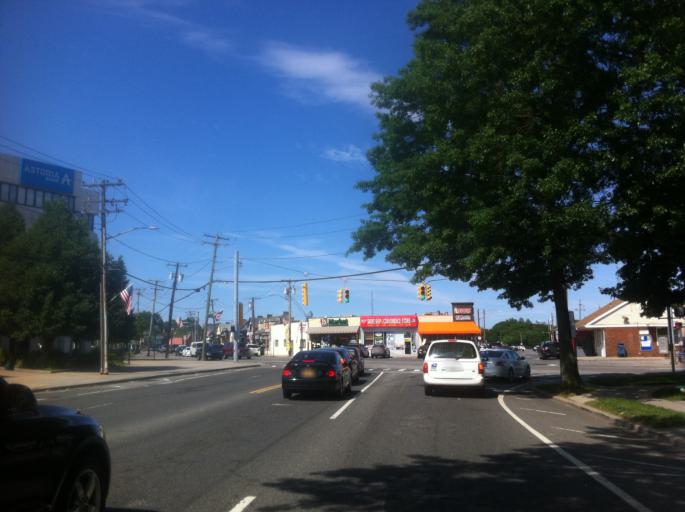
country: US
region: New York
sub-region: Nassau County
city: Syosset
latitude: 40.8236
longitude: -73.5032
